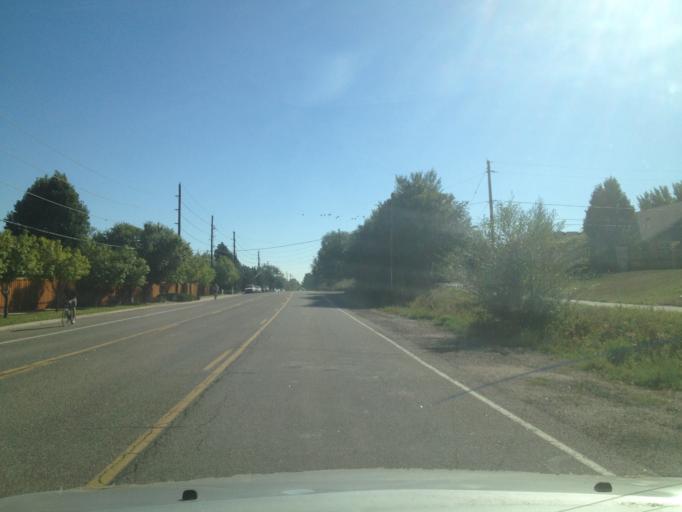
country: US
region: Colorado
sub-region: Jefferson County
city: Applewood
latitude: 39.7617
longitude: -105.1653
